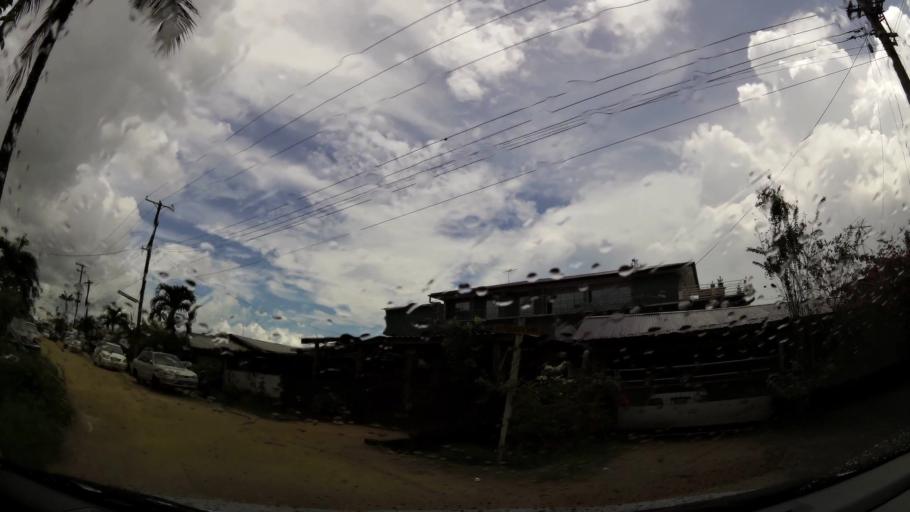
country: SR
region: Paramaribo
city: Paramaribo
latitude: 5.7901
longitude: -55.2003
